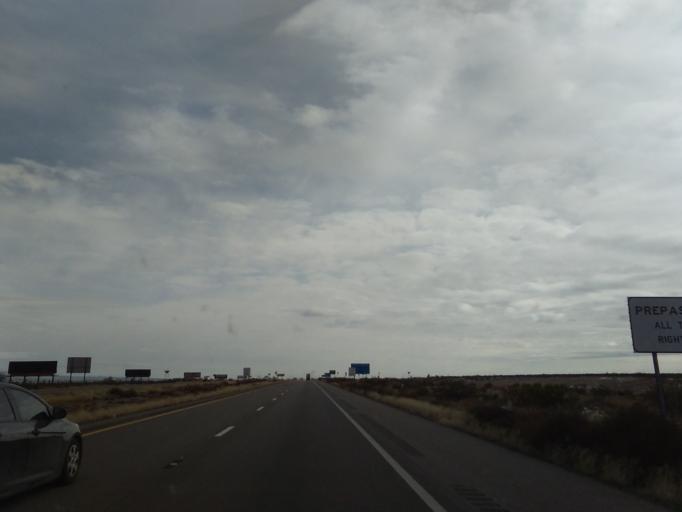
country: US
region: New Mexico
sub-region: Hidalgo County
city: Lordsburg
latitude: 32.3488
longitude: -108.7302
